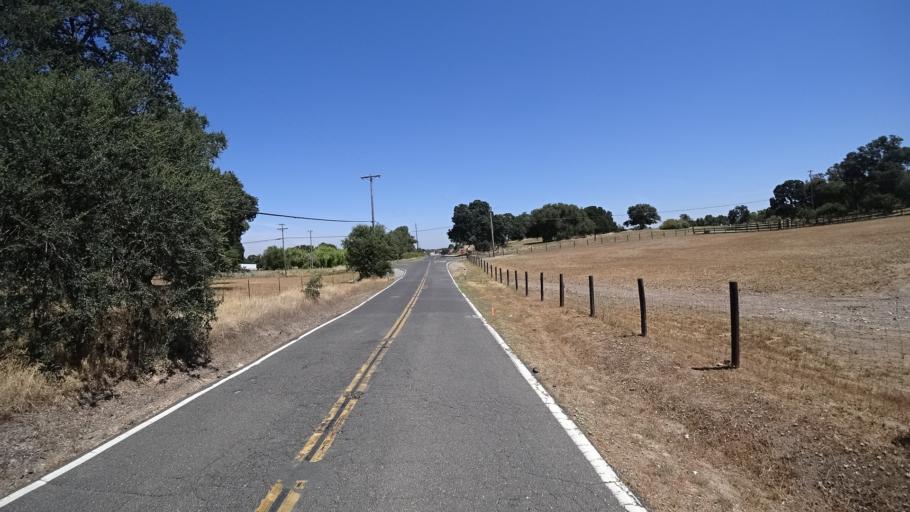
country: US
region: California
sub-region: Calaveras County
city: Rancho Calaveras
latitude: 38.1476
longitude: -120.9448
